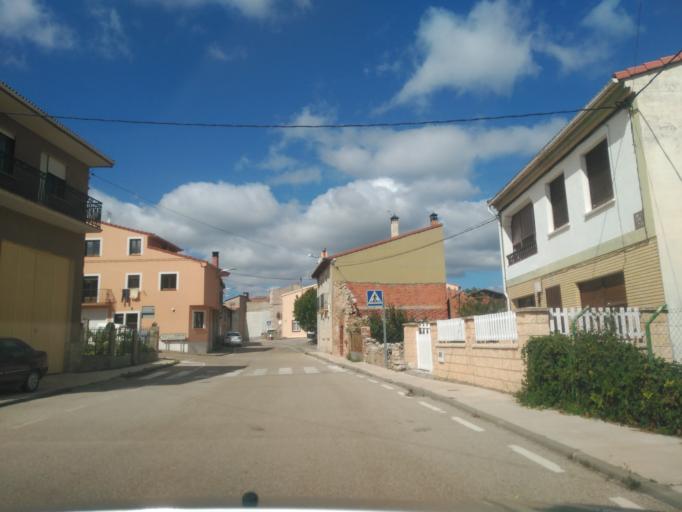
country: ES
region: Castille and Leon
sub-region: Provincia de Soria
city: Espejon
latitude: 41.8301
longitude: -3.2567
